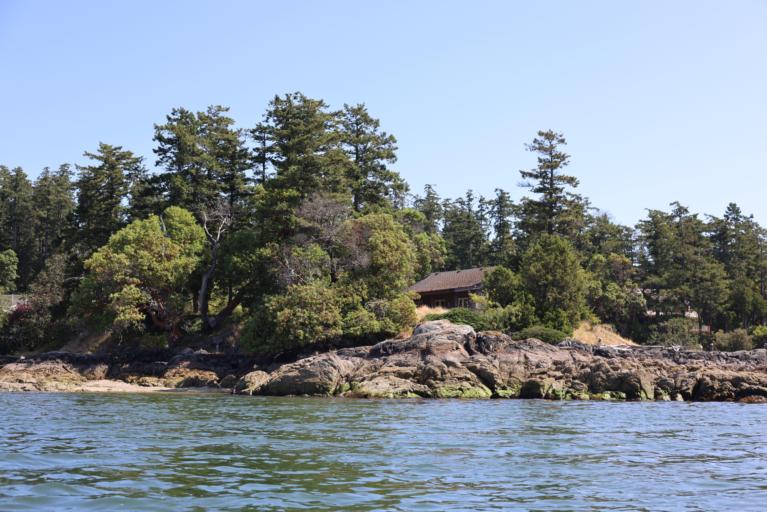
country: CA
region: British Columbia
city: Colwood
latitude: 48.4486
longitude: -123.4404
